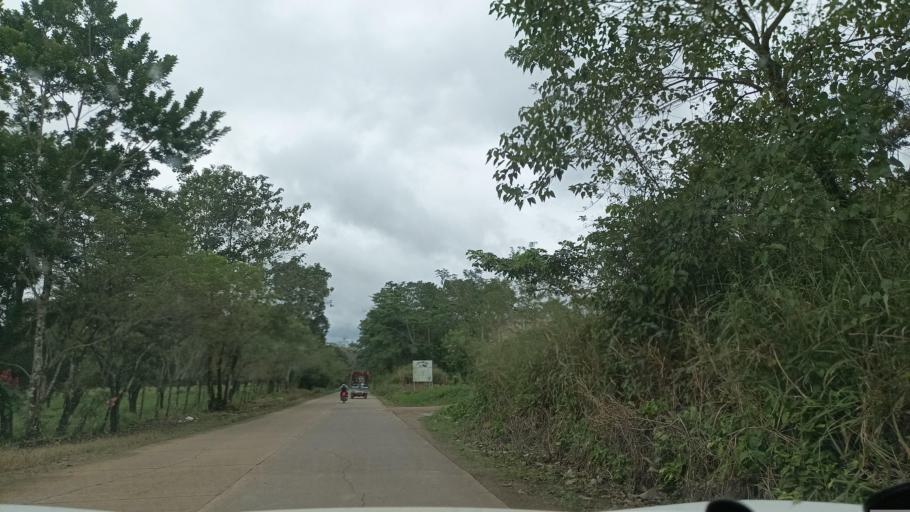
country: MX
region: Veracruz
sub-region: Uxpanapa
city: Poblado 10
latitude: 17.2784
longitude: -94.4759
